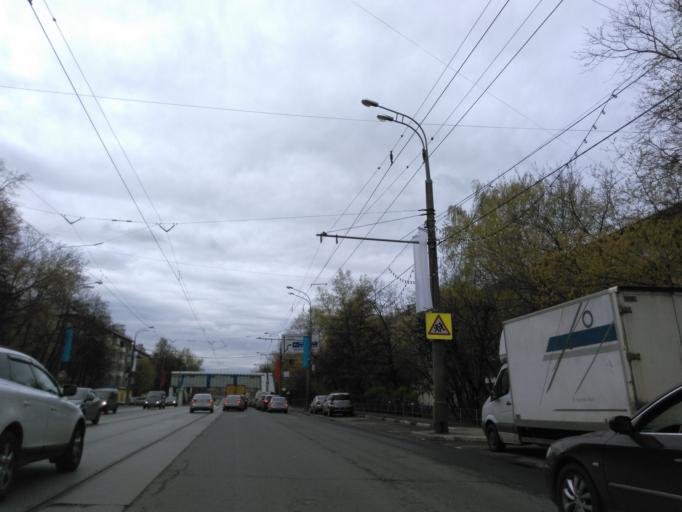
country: RU
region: Moscow
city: Pokrovskoye-Streshnevo
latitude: 55.8262
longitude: 37.4521
